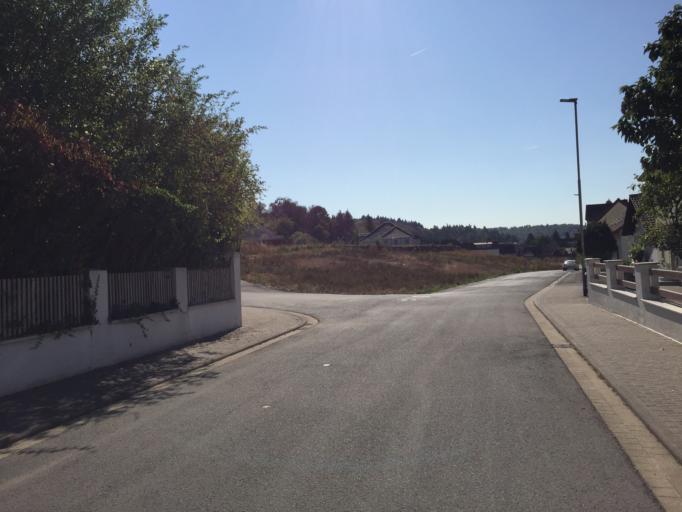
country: DE
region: Hesse
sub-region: Regierungsbezirk Giessen
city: Hungen
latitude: 50.4297
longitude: 8.9357
